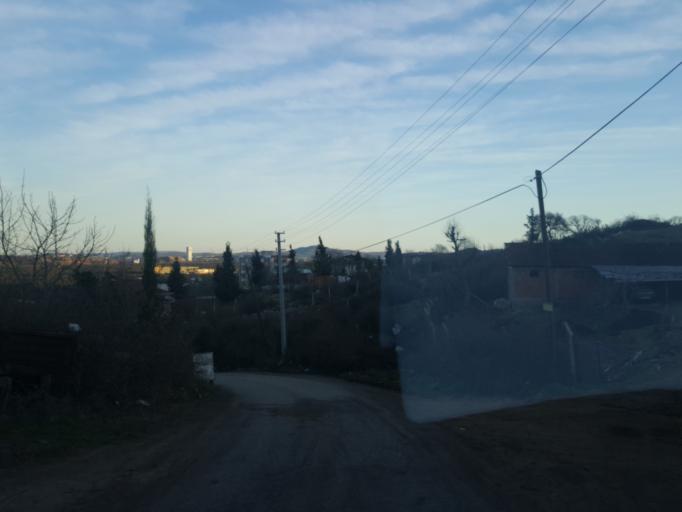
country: TR
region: Kocaeli
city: Tavsanli
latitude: 40.8440
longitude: 29.5564
